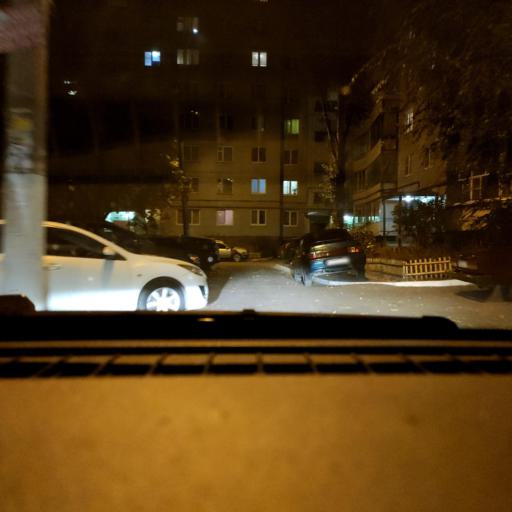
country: RU
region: Voronezj
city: Voronezh
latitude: 51.6424
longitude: 39.2341
